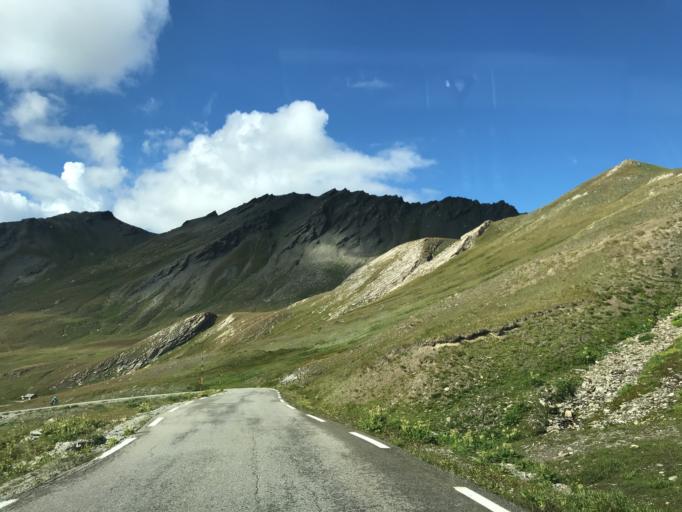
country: IT
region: Piedmont
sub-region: Provincia di Cuneo
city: Pontechianale
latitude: 44.6871
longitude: 6.9789
